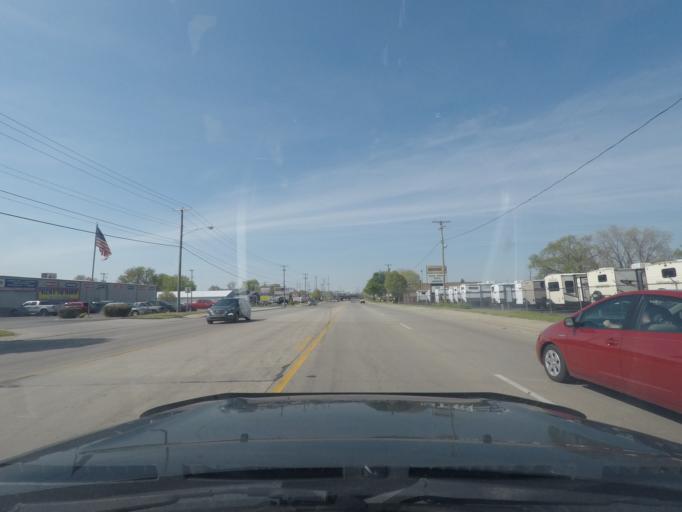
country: US
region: Indiana
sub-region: Elkhart County
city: Elkhart
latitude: 41.6643
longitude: -86.0031
